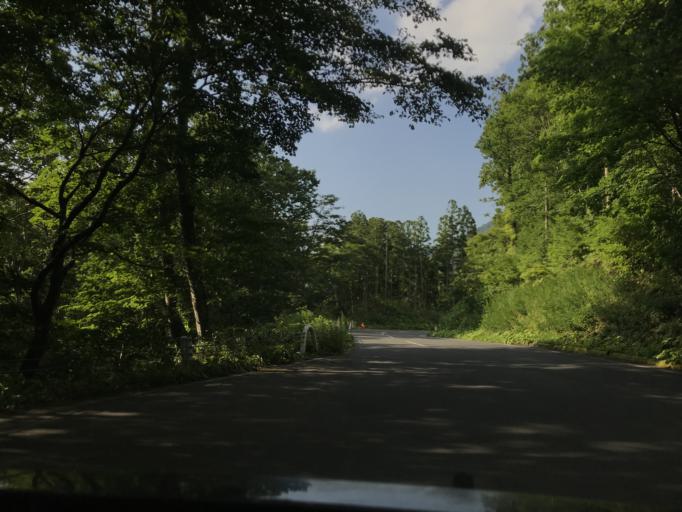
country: JP
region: Iwate
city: Ichinoseki
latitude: 39.0015
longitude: 140.8354
